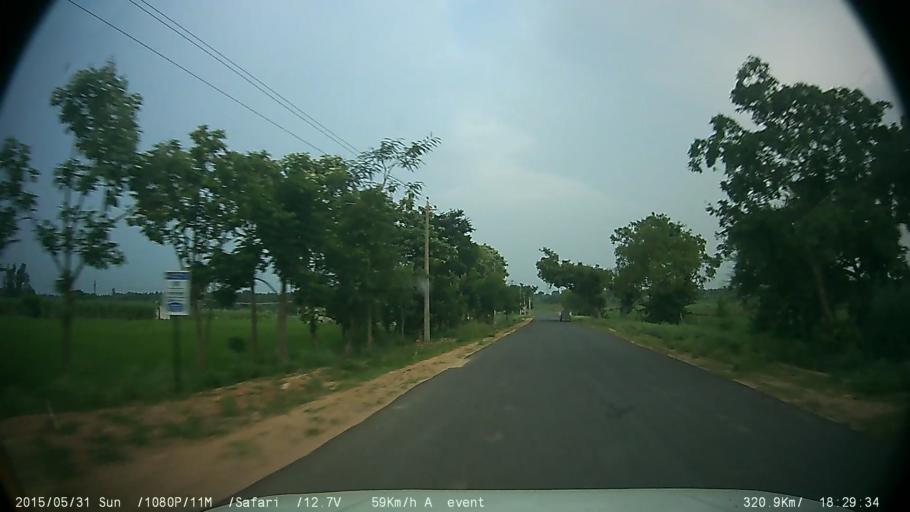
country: IN
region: Karnataka
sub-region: Mysore
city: Nanjangud
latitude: 12.1227
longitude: 76.7315
